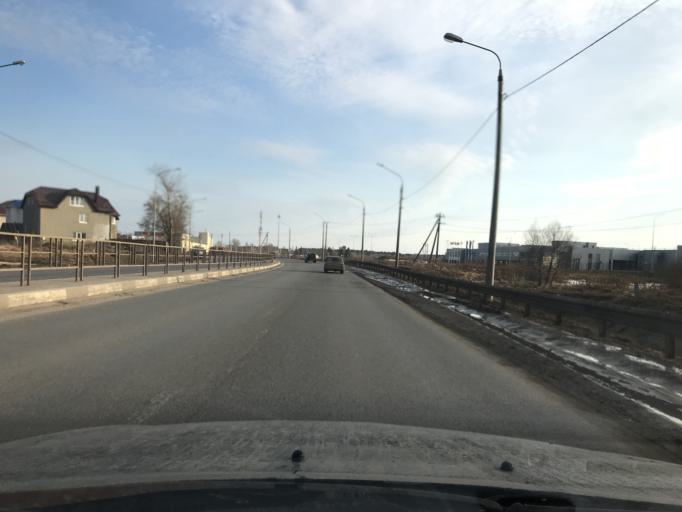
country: RU
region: Kaluga
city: Kaluga
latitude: 54.4721
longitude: 36.2362
